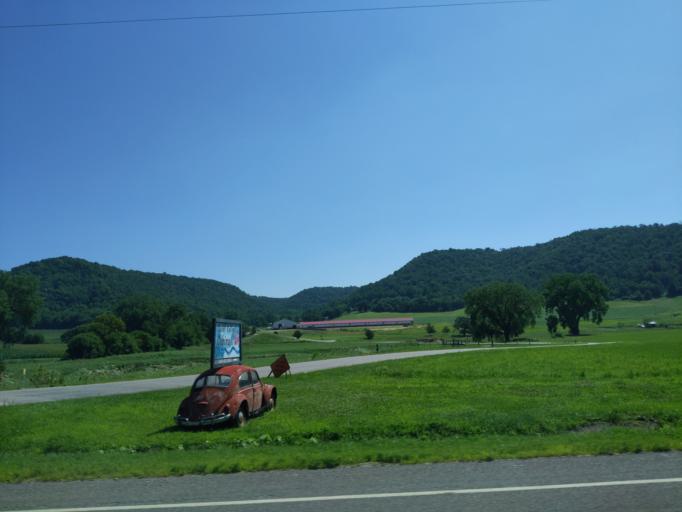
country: US
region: Wisconsin
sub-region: Vernon County
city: Westby
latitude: 43.6835
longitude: -91.0445
